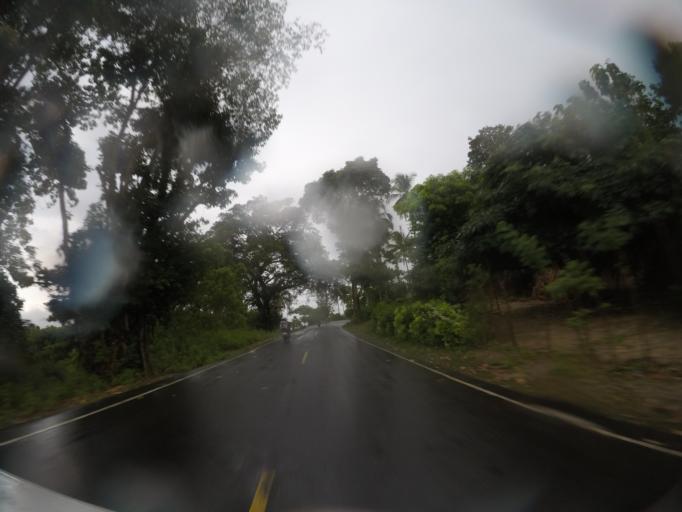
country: TL
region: Bobonaro
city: Maliana
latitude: -8.9662
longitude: 125.0521
